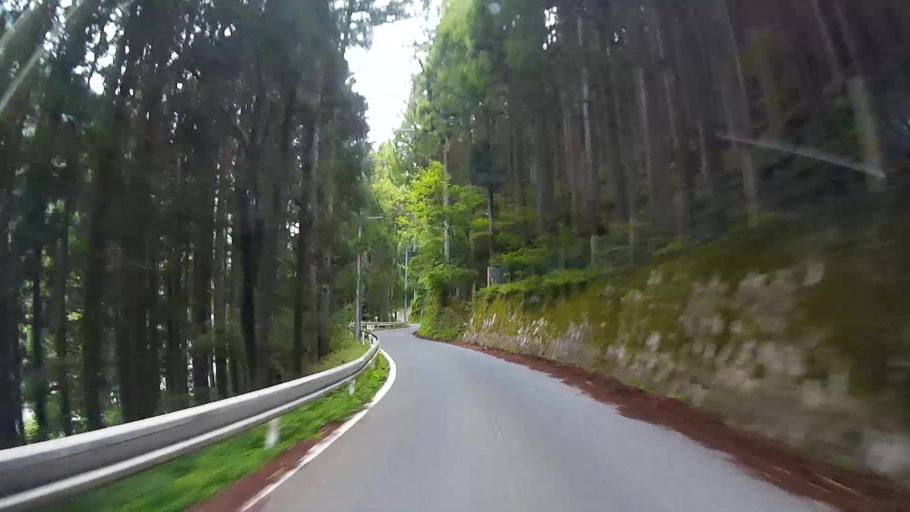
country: JP
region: Saitama
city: Chichibu
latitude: 35.9417
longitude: 138.8910
